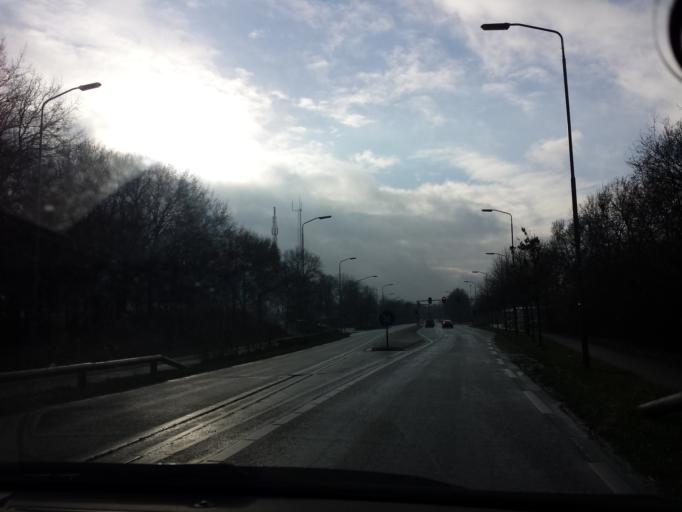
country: NL
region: North Brabant
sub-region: Gemeente Grave
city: Grave
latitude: 51.7557
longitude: 5.7357
